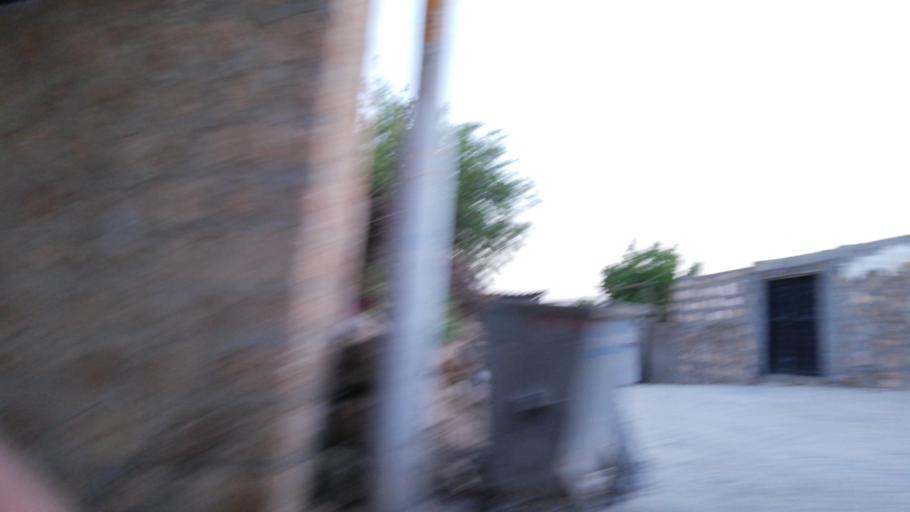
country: TR
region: Mardin
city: Kindirip
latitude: 37.4453
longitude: 41.2215
